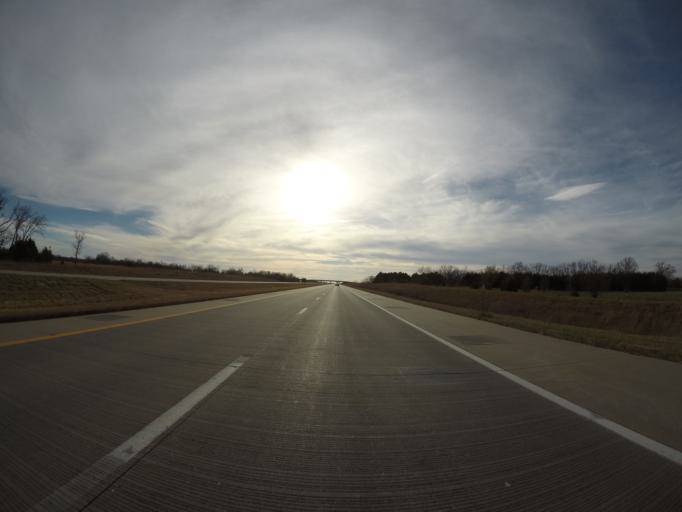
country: US
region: Kansas
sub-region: Franklin County
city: Ottawa
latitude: 38.6564
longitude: -95.1897
